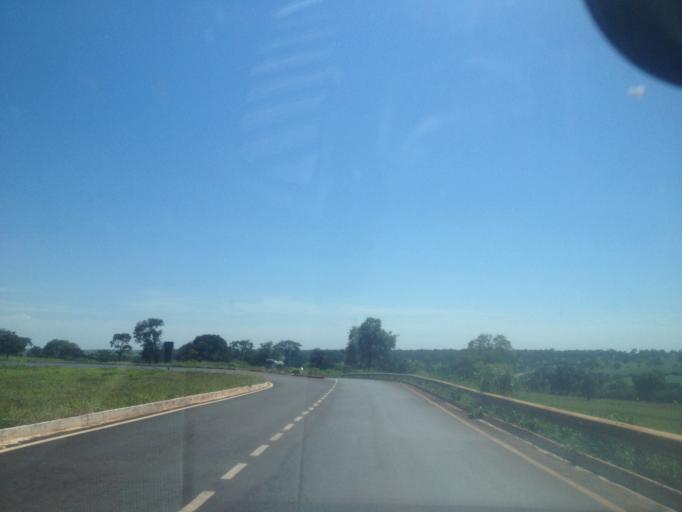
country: BR
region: Minas Gerais
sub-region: Santa Vitoria
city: Santa Vitoria
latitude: -18.8761
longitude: -50.1216
